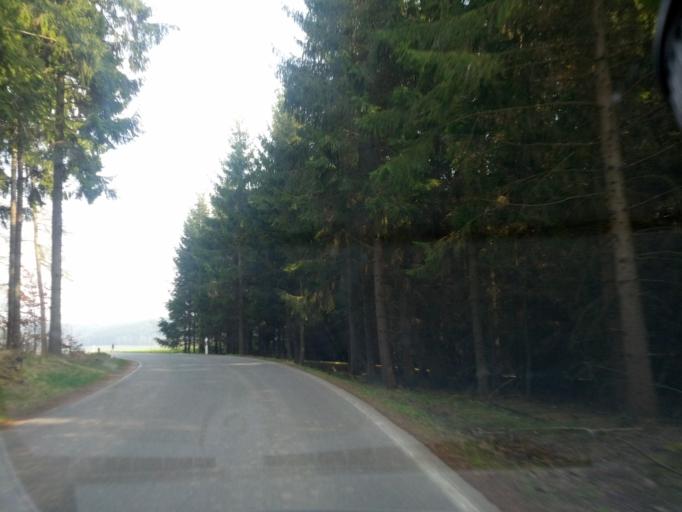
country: DE
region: Saxony
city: Stutzengrun
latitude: 50.5763
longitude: 12.5216
